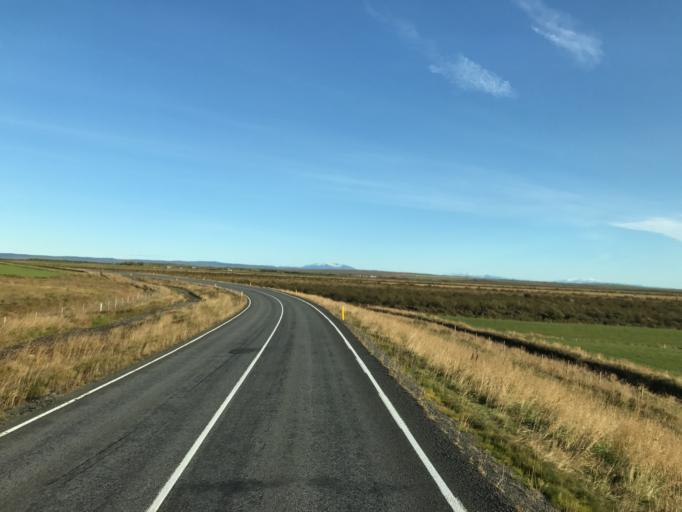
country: IS
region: South
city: Selfoss
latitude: 64.2237
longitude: -20.6190
